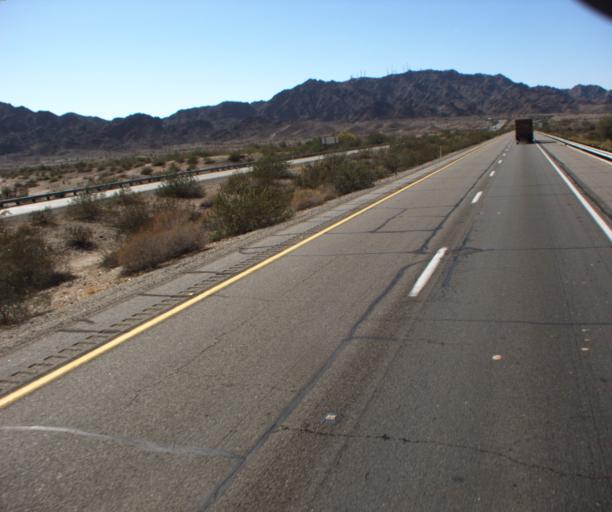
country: US
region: Arizona
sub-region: Yuma County
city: Fortuna Foothills
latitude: 32.6692
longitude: -114.2915
